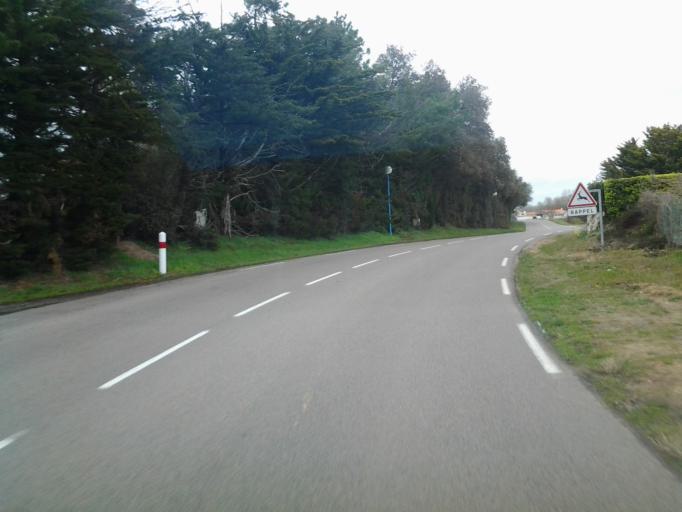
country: FR
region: Pays de la Loire
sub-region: Departement de la Vendee
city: Longeville-sur-Mer
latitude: 46.3950
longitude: -1.4851
